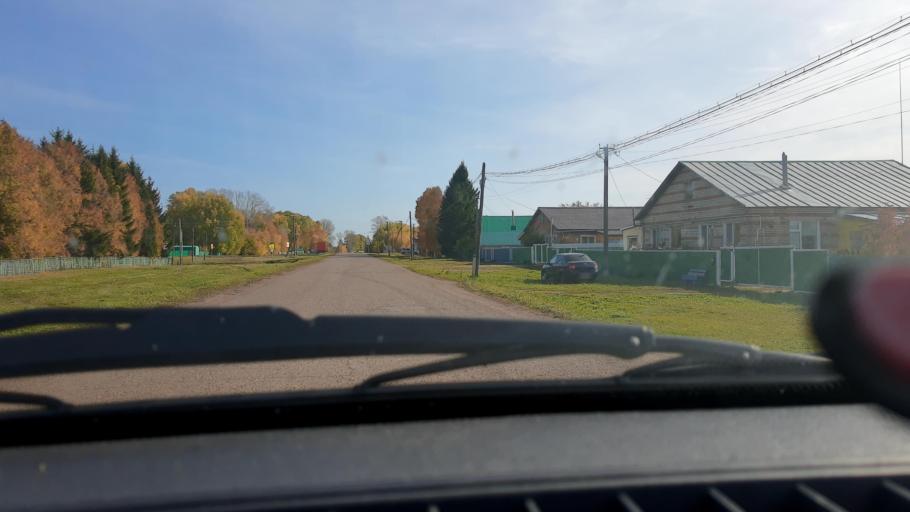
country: RU
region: Bashkortostan
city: Chekmagush
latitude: 54.8774
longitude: 54.6107
